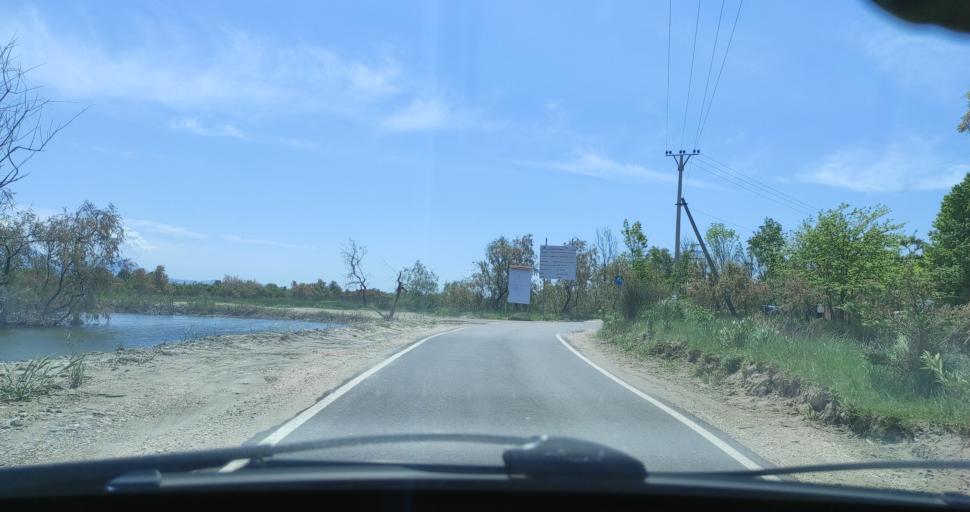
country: AL
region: Lezhe
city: Lezhe
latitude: 41.7530
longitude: 19.6076
